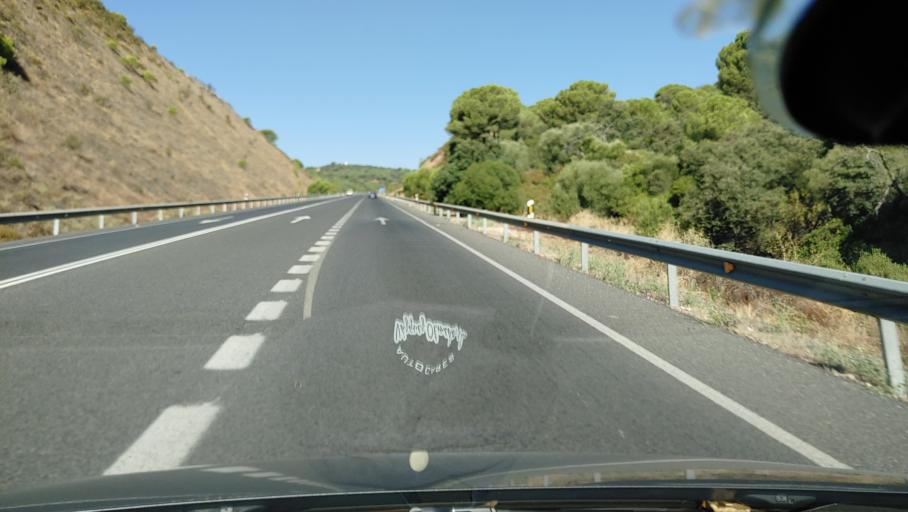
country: ES
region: Andalusia
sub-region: Province of Cordoba
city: Cordoba
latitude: 37.9801
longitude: -4.7802
